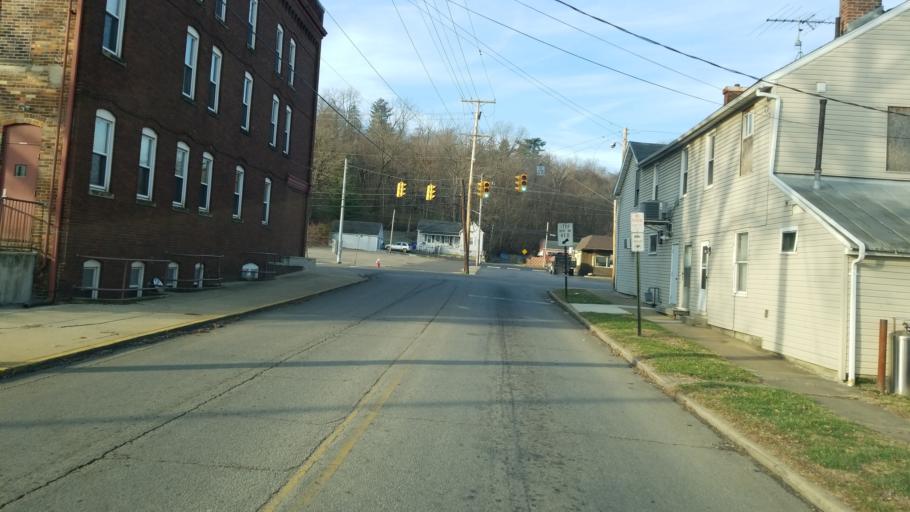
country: US
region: Ohio
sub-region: Ross County
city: Chillicothe
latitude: 39.3259
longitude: -82.9797
